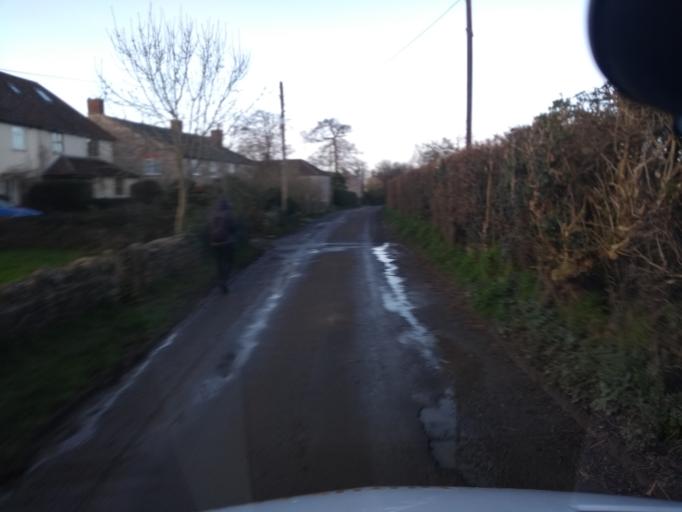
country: GB
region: England
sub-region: Somerset
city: Wedmore
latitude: 51.2278
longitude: -2.8404
